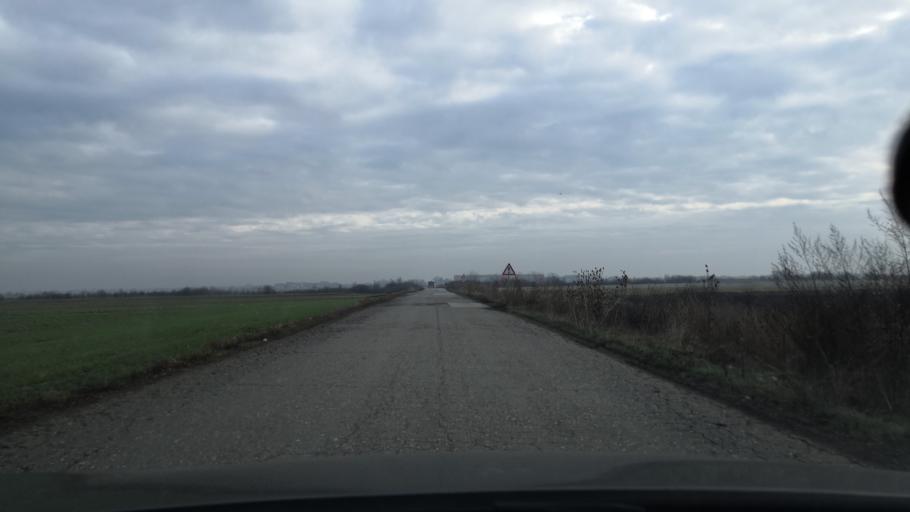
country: RS
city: Ugrinovci
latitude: 44.8814
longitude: 20.1558
